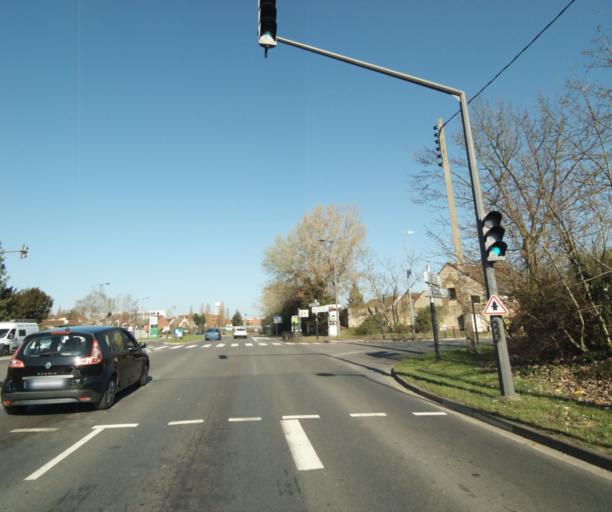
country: FR
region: Ile-de-France
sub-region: Departement du Val-d'Oise
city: Cergy
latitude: 49.0297
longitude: 2.0692
